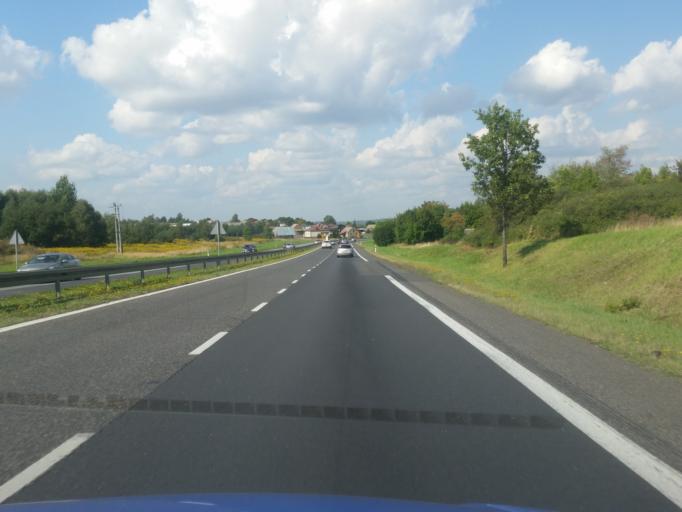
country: PL
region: Silesian Voivodeship
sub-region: Powiat myszkowski
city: Kozieglowy
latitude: 50.5669
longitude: 19.1697
